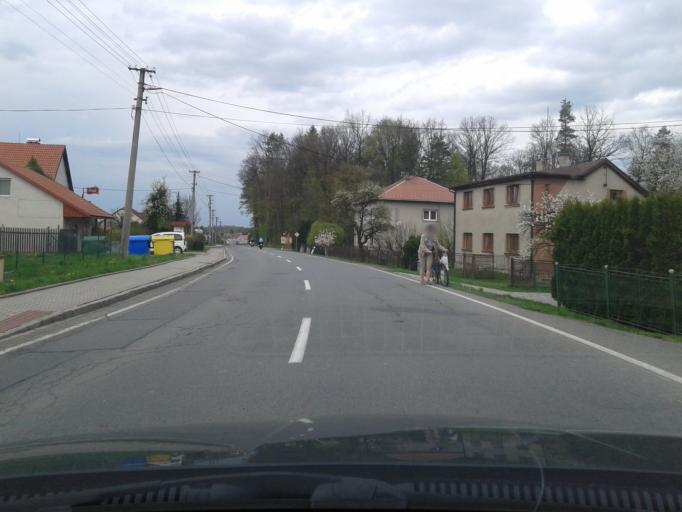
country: CZ
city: Vaclavovice
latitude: 49.7494
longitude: 18.3787
